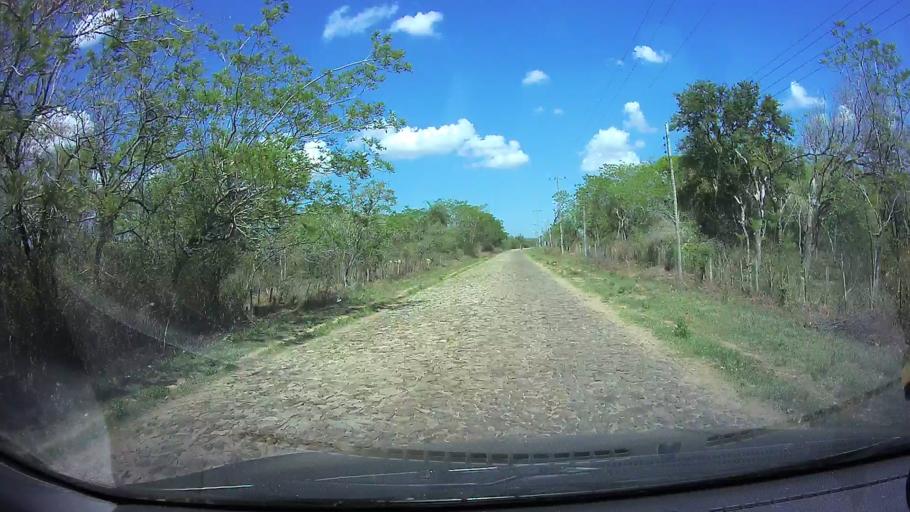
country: PY
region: Cordillera
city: Emboscada
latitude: -25.1160
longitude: -57.2837
